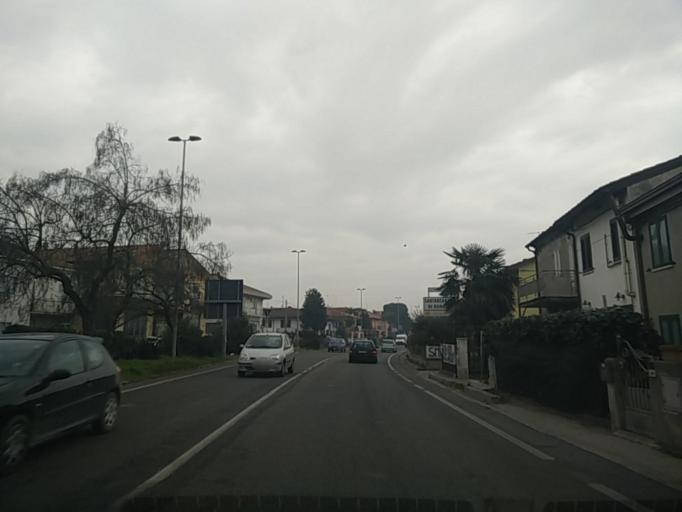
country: IT
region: Emilia-Romagna
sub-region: Provincia di Rimini
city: Santa Giustina
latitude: 44.0683
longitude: 12.4799
